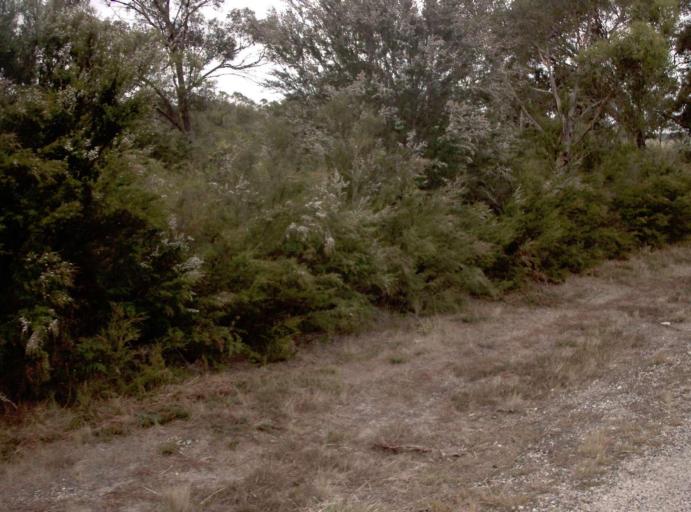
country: AU
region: Victoria
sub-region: Wellington
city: Sale
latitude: -38.1342
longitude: 147.4176
